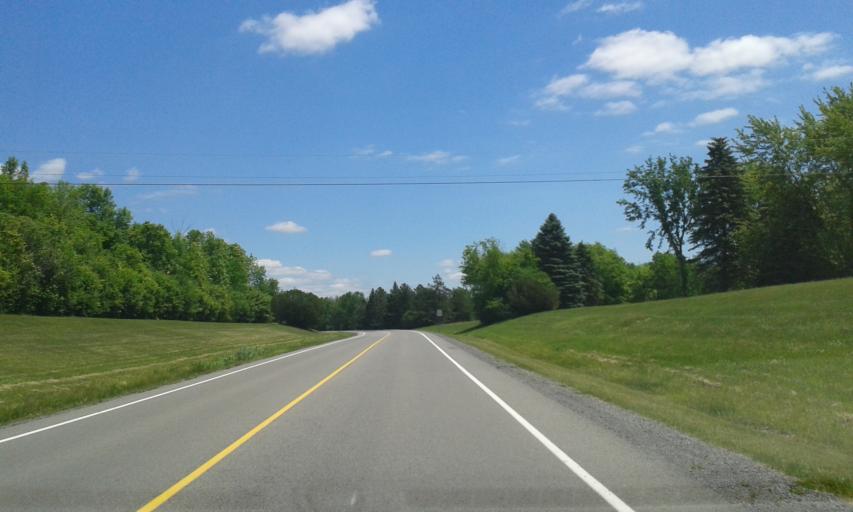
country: US
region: New York
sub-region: St. Lawrence County
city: Massena
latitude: 44.9945
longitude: -74.9495
